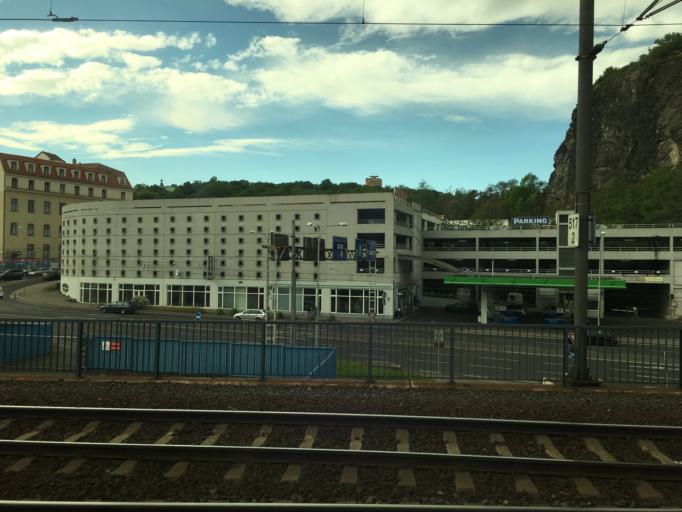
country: CZ
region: Ustecky
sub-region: Okres Usti nad Labem
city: Usti nad Labem
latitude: 50.6605
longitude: 14.0469
